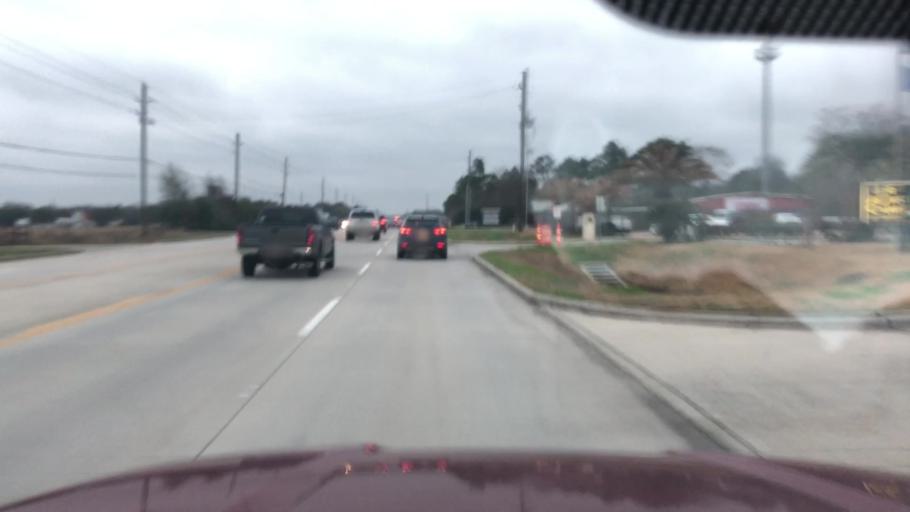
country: US
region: Texas
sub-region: Harris County
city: Tomball
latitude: 30.0496
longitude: -95.5392
